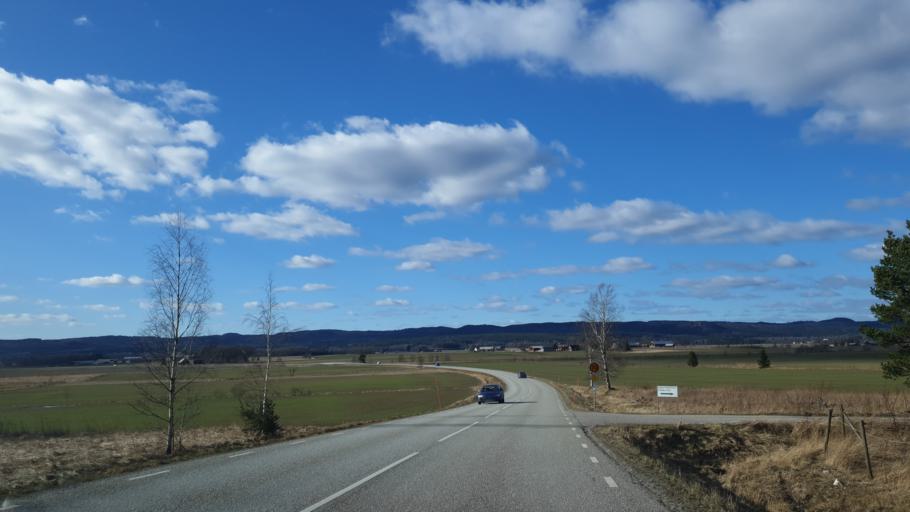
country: SE
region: OErebro
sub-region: Orebro Kommun
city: Garphyttan
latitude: 59.3385
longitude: 15.0619
